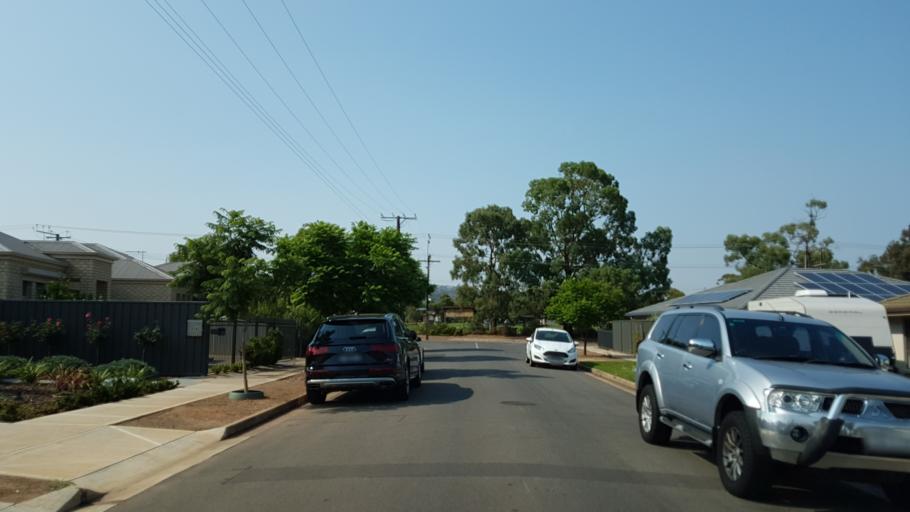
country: AU
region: South Australia
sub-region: Holdfast Bay
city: Seacliff Park
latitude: -35.0216
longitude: 138.5371
